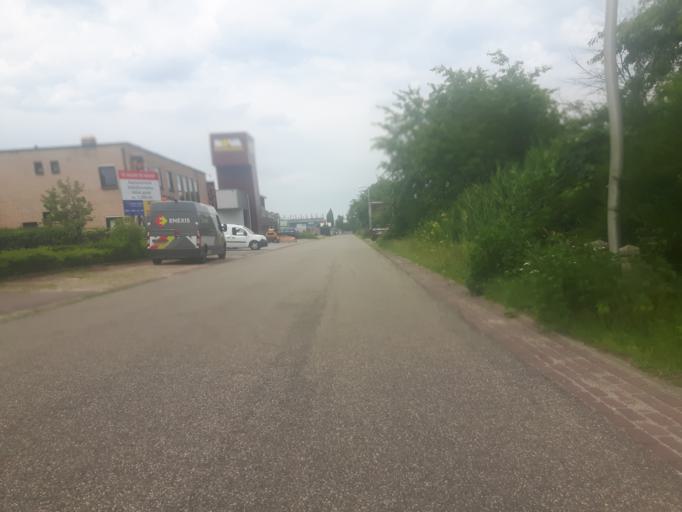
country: NL
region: Overijssel
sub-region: Gemeente Enschede
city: Enschede
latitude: 52.2292
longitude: 6.8514
